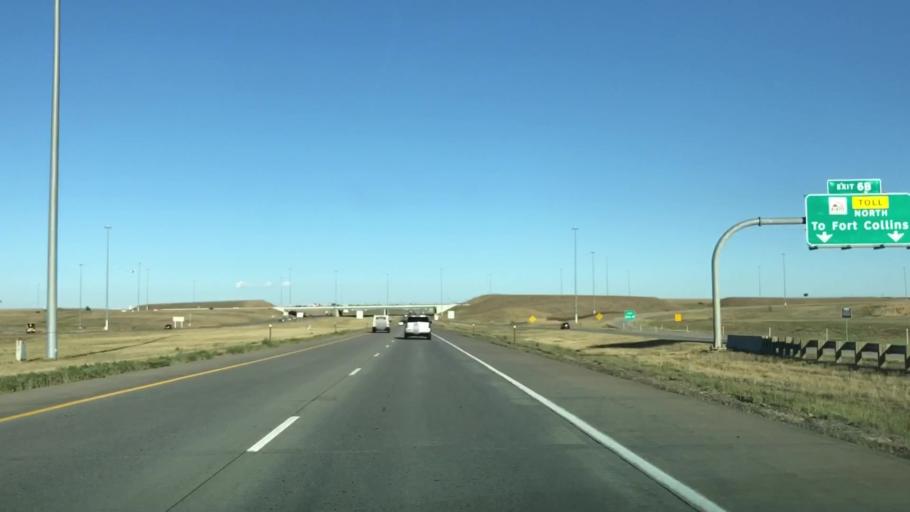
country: US
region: Colorado
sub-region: Adams County
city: Aurora
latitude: 39.8339
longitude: -104.7561
